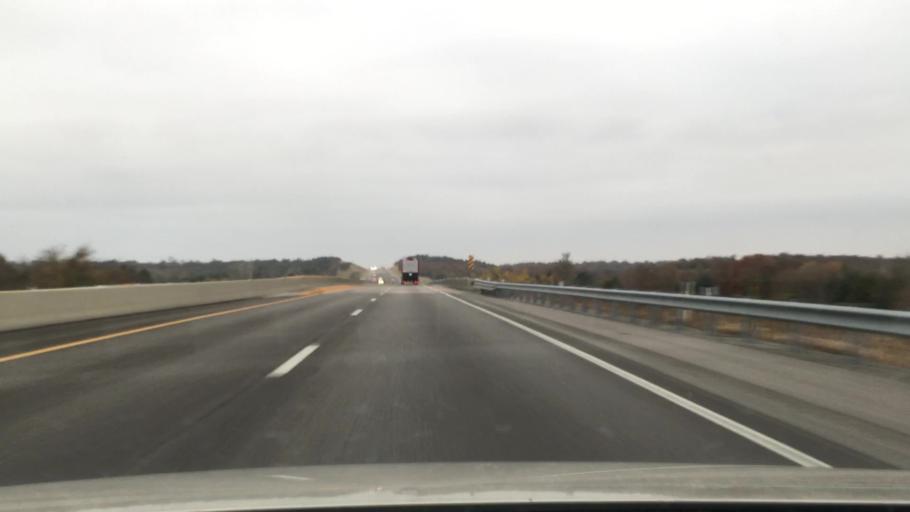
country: US
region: Oklahoma
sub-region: Lincoln County
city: Stroud
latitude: 35.7396
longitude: -96.7698
